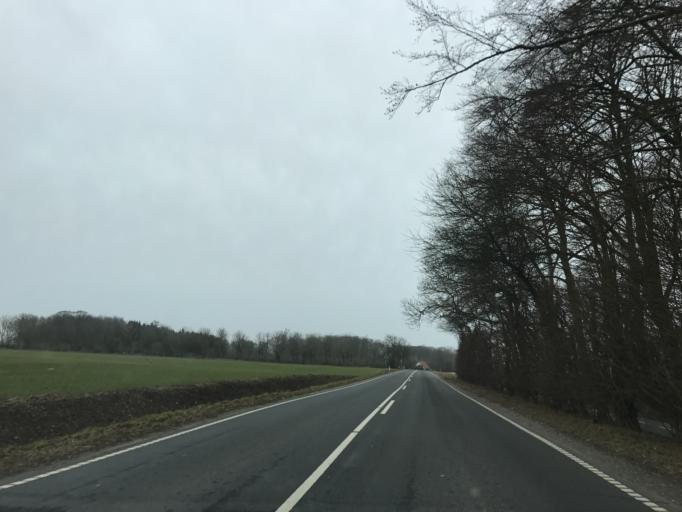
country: DK
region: South Denmark
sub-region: Langeland Kommune
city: Rudkobing
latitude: 54.9535
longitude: 10.7790
